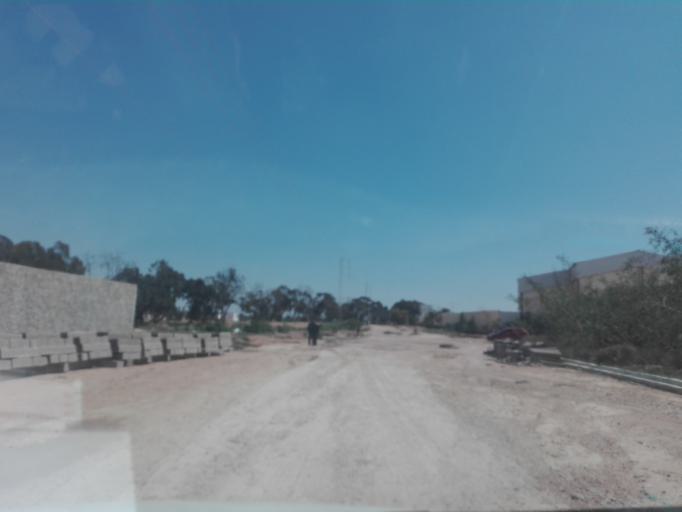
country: TN
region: Safaqis
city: Sfax
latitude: 34.7293
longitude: 10.5208
